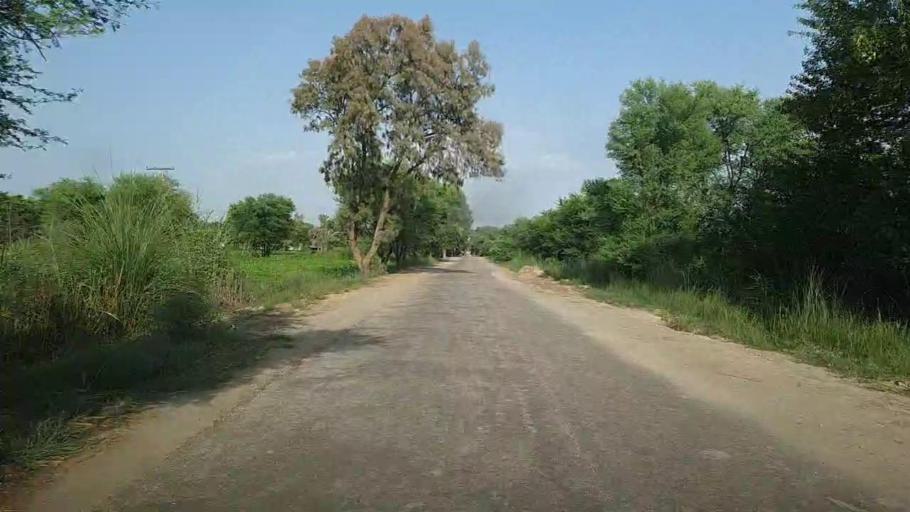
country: PK
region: Sindh
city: Khairpur
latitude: 28.0747
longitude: 69.8195
